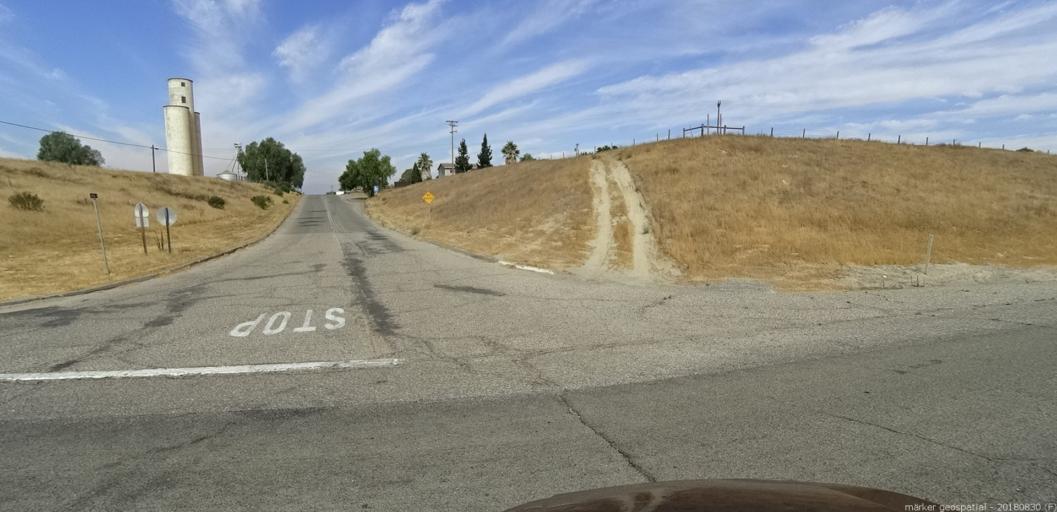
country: US
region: California
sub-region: Monterey County
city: King City
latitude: 36.1278
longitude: -121.0147
